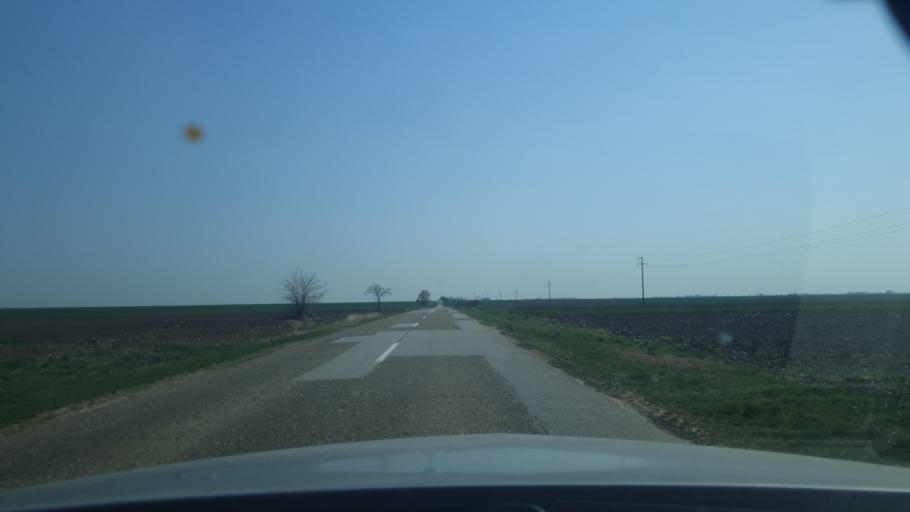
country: RS
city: Sasinci
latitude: 45.0416
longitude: 19.7307
